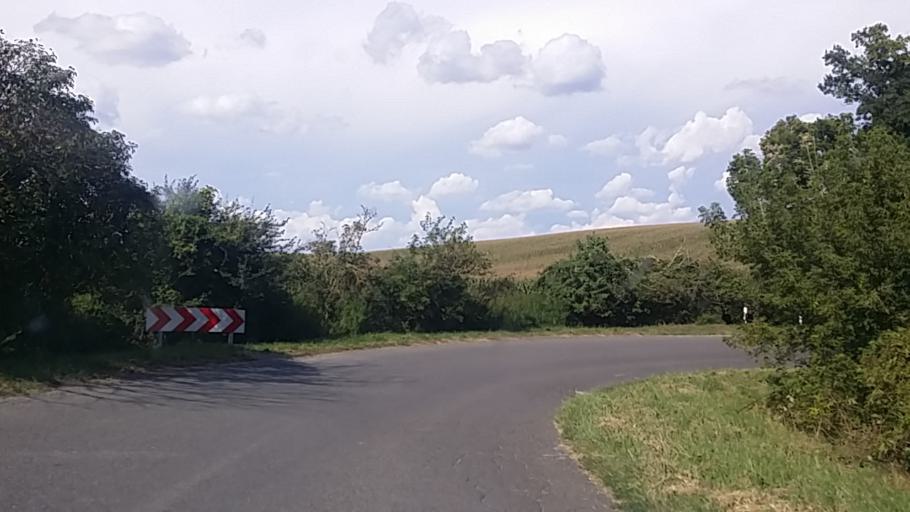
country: HU
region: Tolna
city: Gyonk
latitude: 46.5389
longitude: 18.4579
